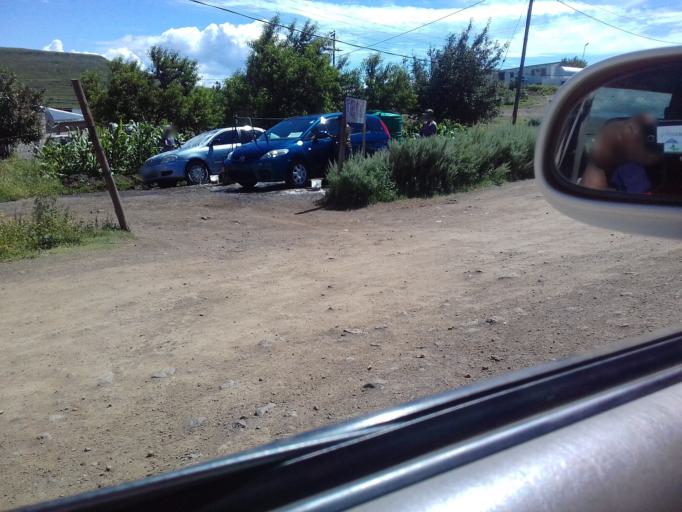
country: LS
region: Thaba-Tseka
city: Thaba-Tseka
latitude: -29.5155
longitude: 28.5935
